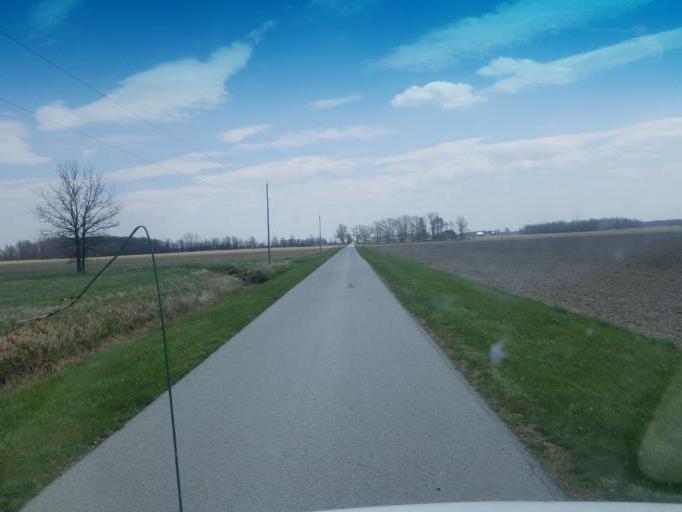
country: US
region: Ohio
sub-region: Hardin County
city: Forest
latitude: 40.7744
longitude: -83.4926
